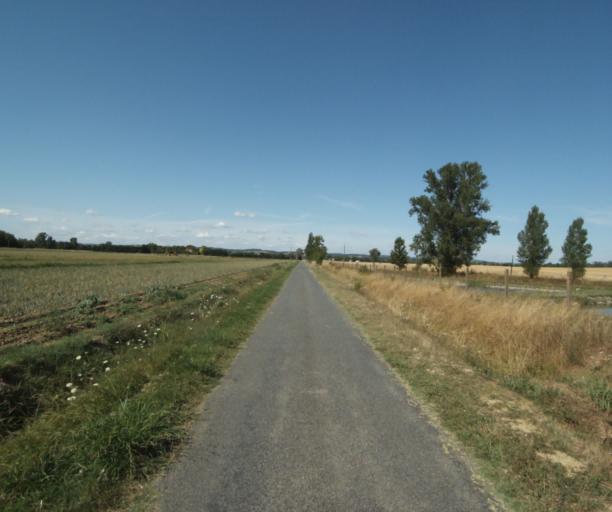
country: FR
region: Midi-Pyrenees
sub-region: Departement de la Haute-Garonne
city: Revel
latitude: 43.5009
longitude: 1.9674
